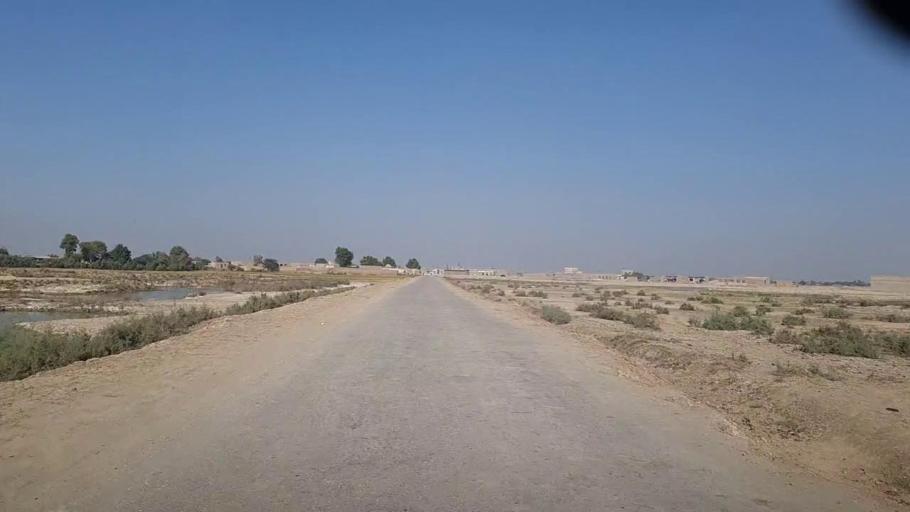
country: PK
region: Sindh
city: Tangwani
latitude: 28.2592
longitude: 68.9982
